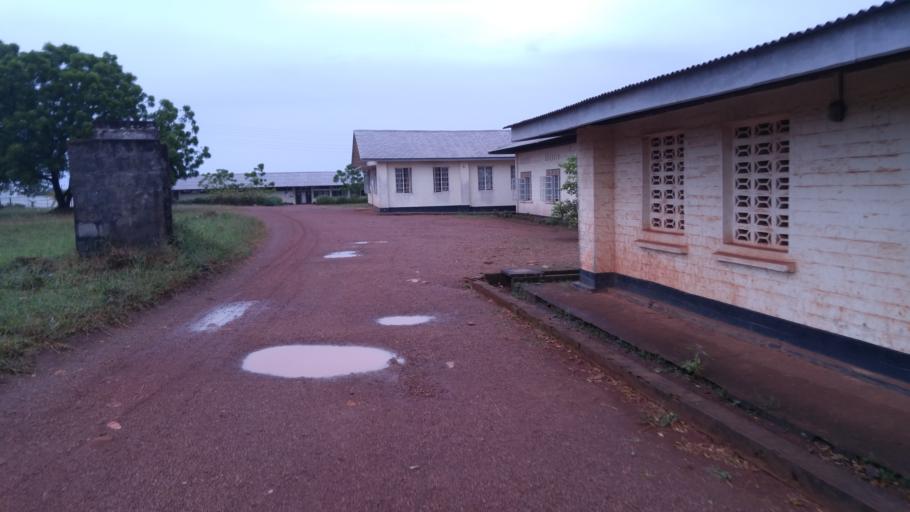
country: SL
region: Southern Province
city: Largo
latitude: 8.1147
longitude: -12.0692
